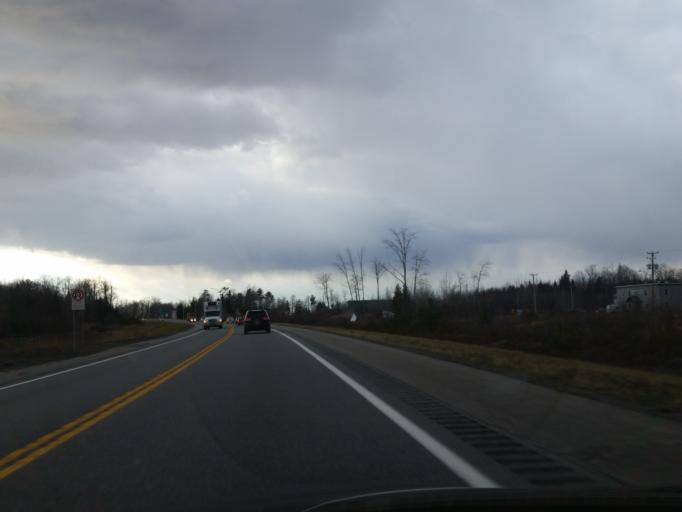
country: CA
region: Quebec
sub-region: Laurentides
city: Lachute
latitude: 45.6396
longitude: -74.3090
